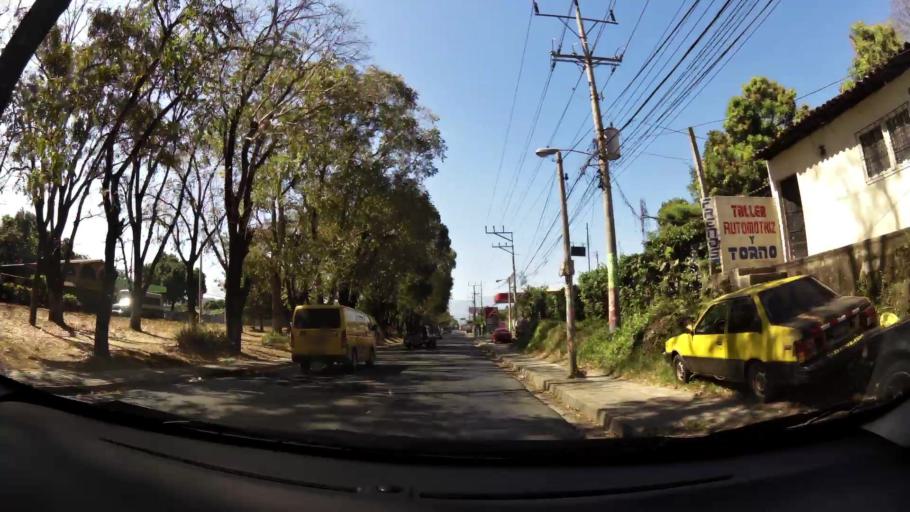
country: SV
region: La Libertad
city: Santa Tecla
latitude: 13.7259
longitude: -89.3740
